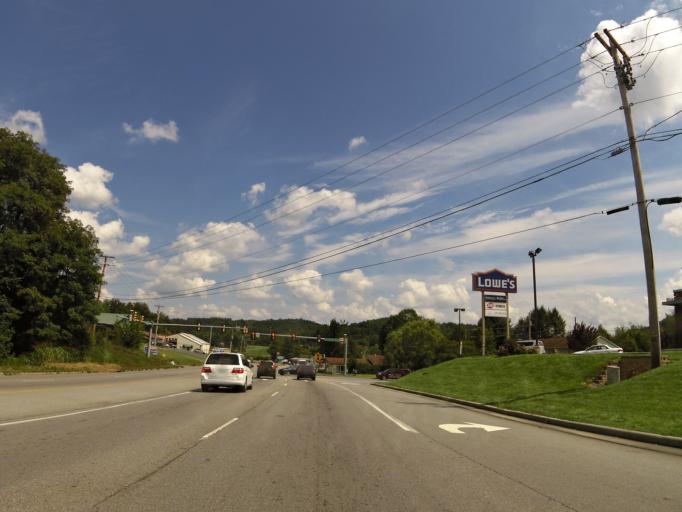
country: US
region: Virginia
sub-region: Washington County
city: Abingdon
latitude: 36.7128
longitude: -81.9306
